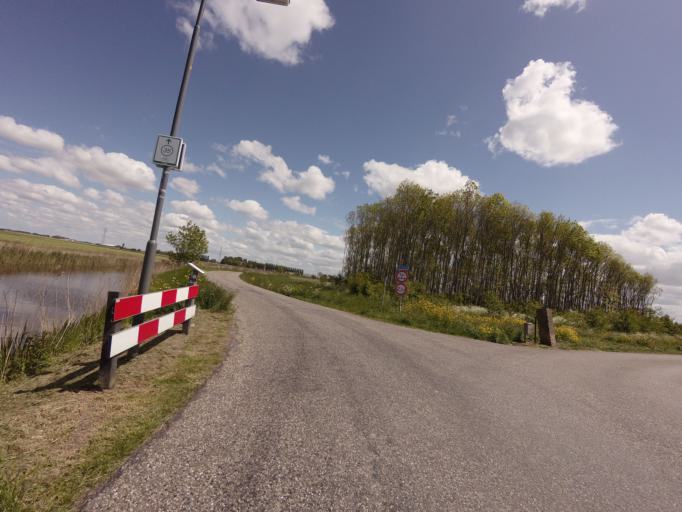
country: NL
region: Friesland
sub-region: Gemeente Franekeradeel
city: Franeker
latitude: 53.1474
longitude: 5.4903
